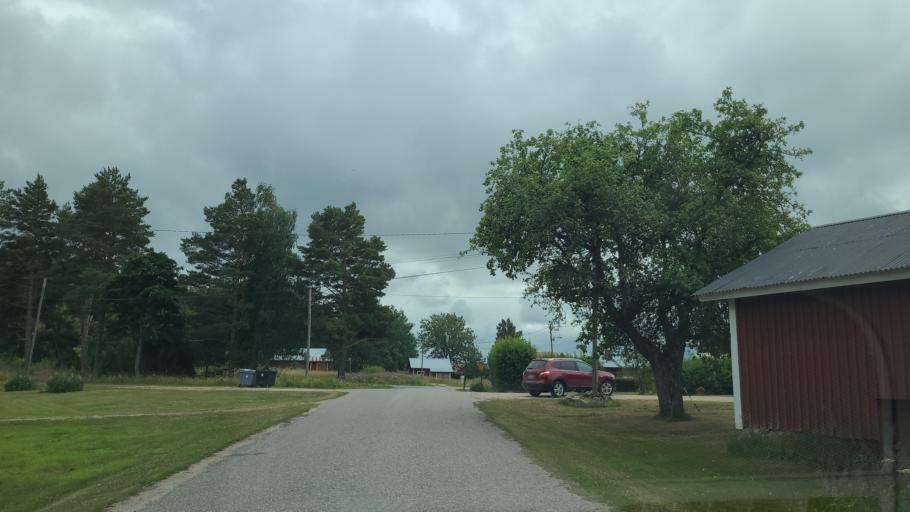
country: FI
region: Varsinais-Suomi
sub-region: Aboland-Turunmaa
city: Dragsfjaerd
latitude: 60.0828
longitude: 22.4138
